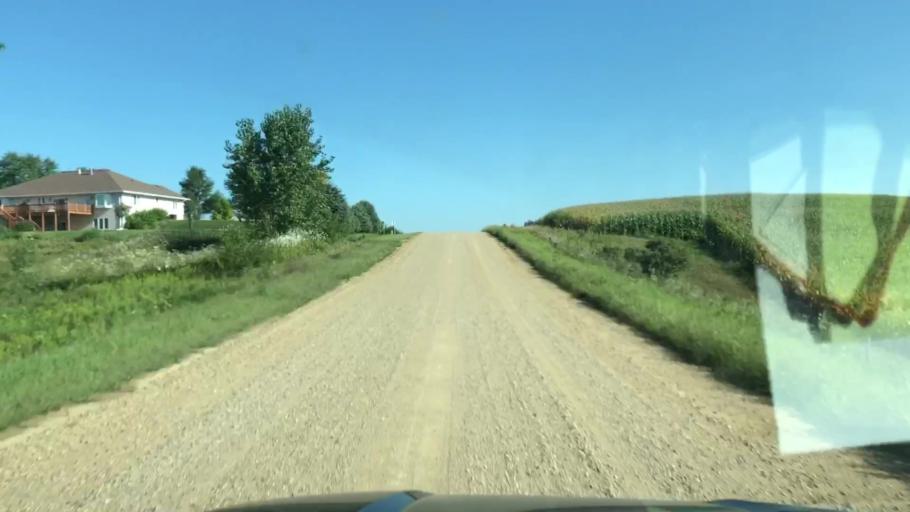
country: US
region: Iowa
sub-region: Woodbury County
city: Sergeant Bluff
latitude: 42.4709
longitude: -96.2921
